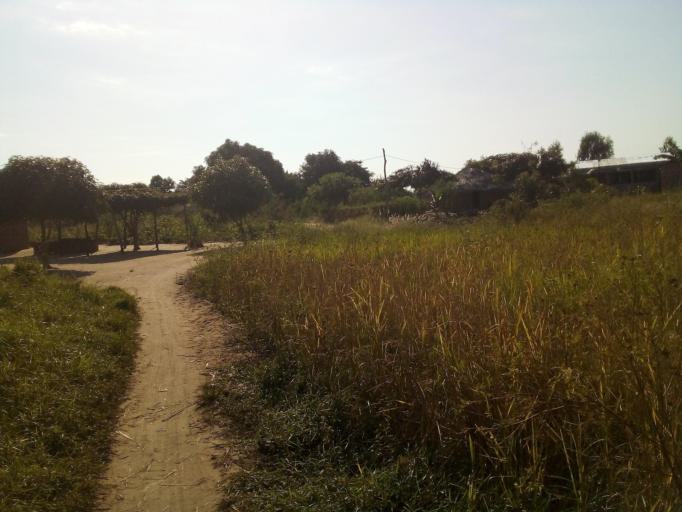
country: MZ
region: Zambezia
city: Quelimane
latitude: -17.5559
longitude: 36.7001
